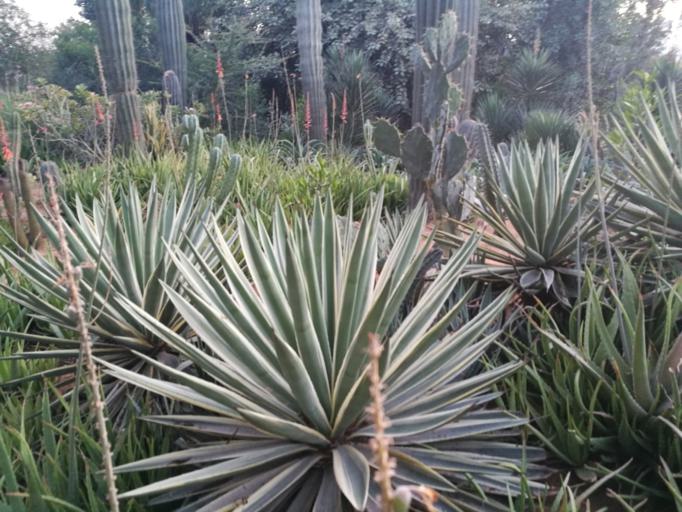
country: AE
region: Ash Shariqah
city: Sharjah
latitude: 25.3336
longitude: 55.3858
